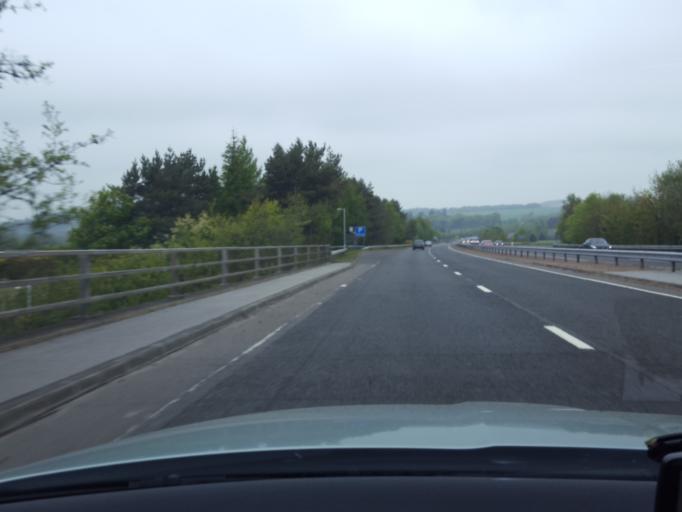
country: GB
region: Scotland
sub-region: Angus
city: Forfar
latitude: 56.5865
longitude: -2.9133
